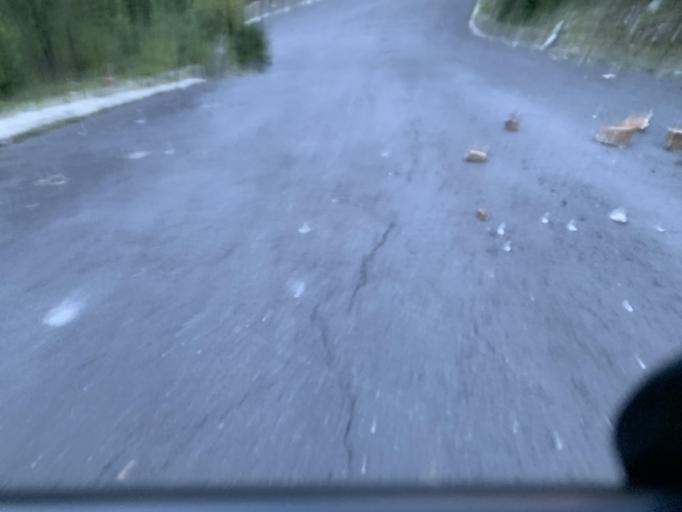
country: MX
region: Nuevo Leon
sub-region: Juarez
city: Bosques de San Pedro
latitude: 25.5197
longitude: -100.1840
